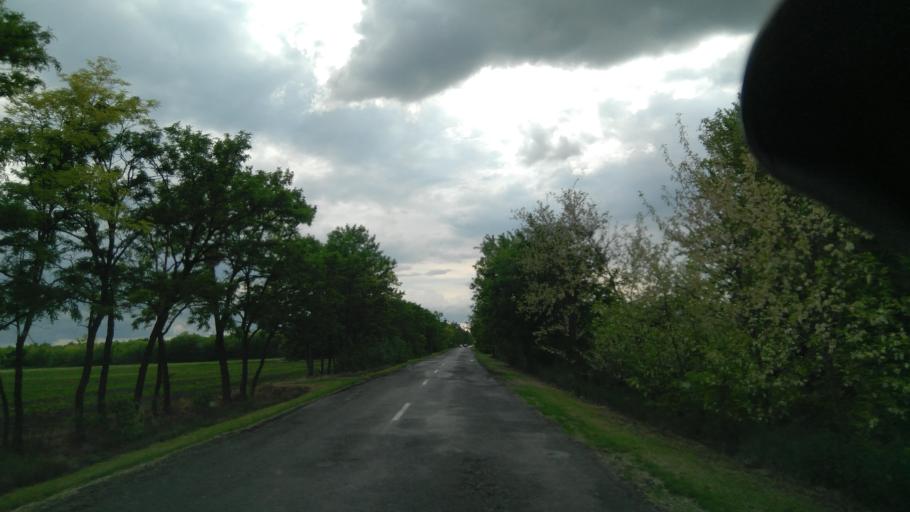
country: HU
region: Bekes
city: Gadoros
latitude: 46.6654
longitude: 20.5809
